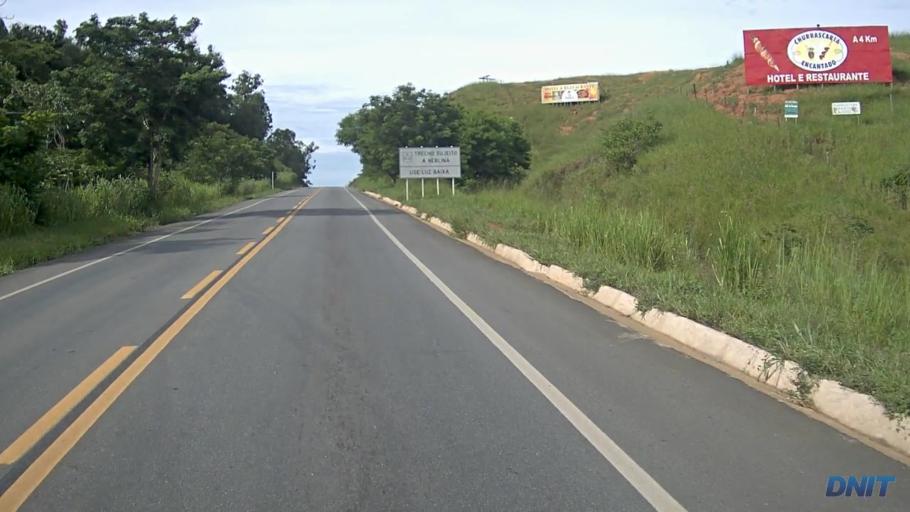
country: BR
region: Minas Gerais
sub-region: Belo Oriente
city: Belo Oriente
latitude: -19.2521
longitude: -42.3399
